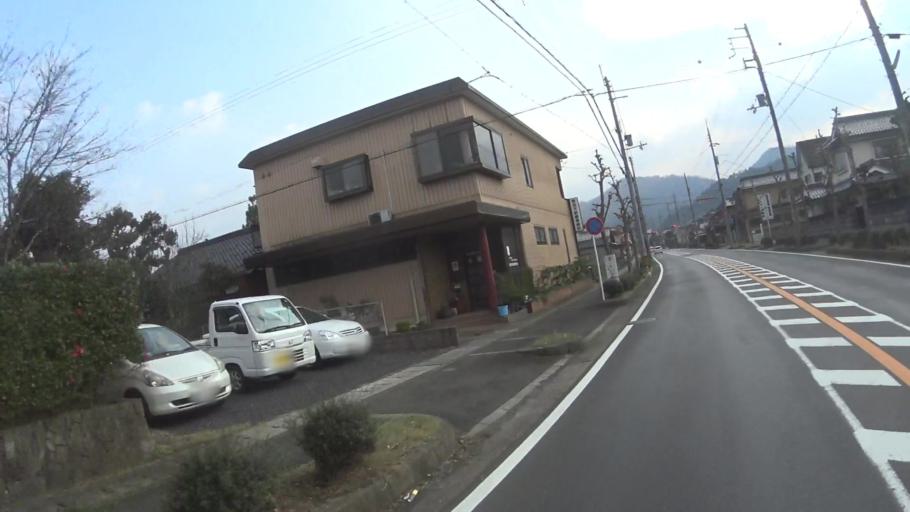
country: JP
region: Kyoto
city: Maizuru
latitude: 35.4588
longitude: 135.3969
